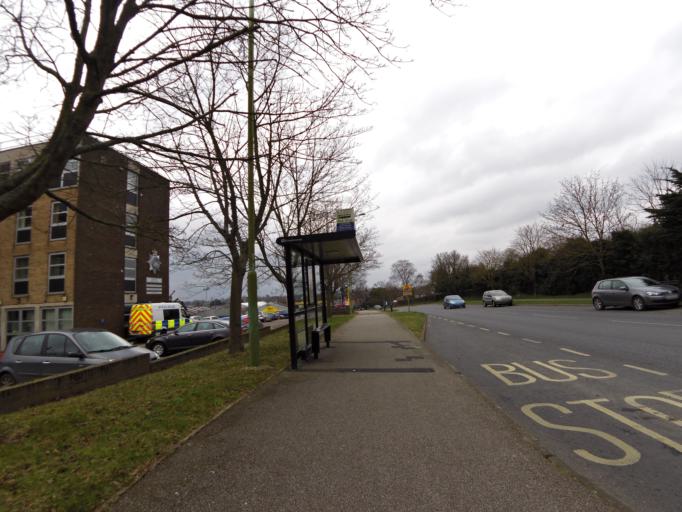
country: GB
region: England
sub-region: Suffolk
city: Halesworth
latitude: 52.3479
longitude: 1.5044
